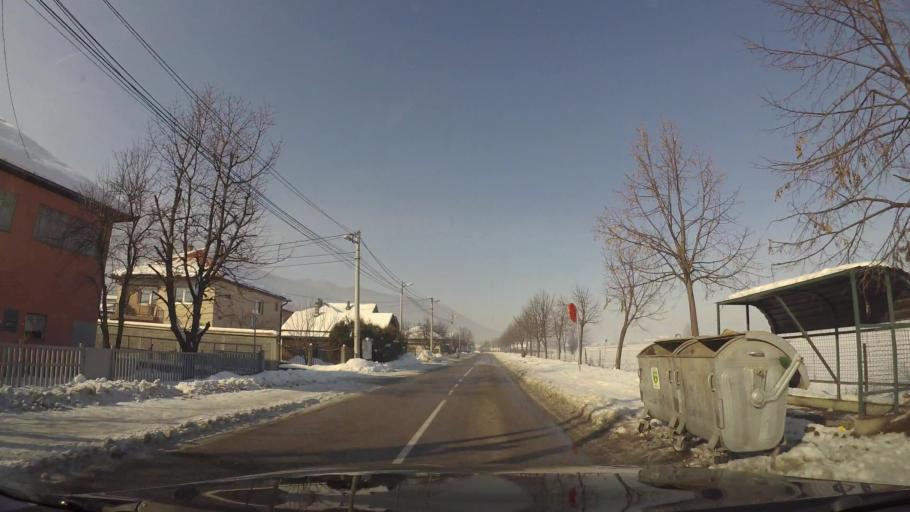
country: BA
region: Federation of Bosnia and Herzegovina
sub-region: Kanton Sarajevo
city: Sarajevo
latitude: 43.8033
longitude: 18.3057
